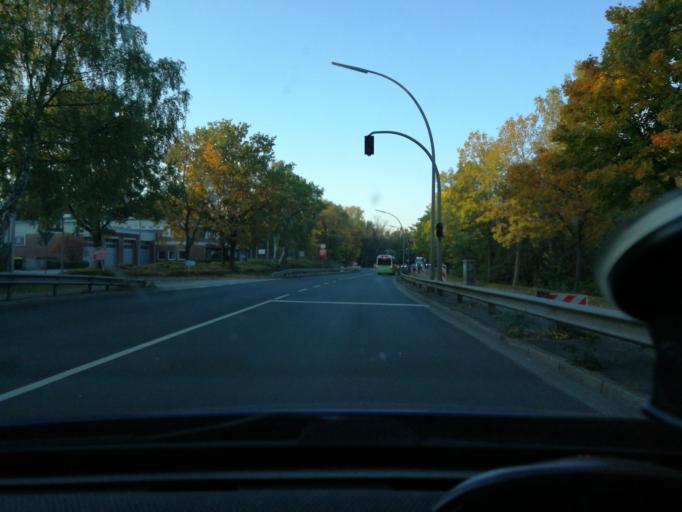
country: DE
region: Hamburg
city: Altona
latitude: 53.4755
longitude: 9.8996
